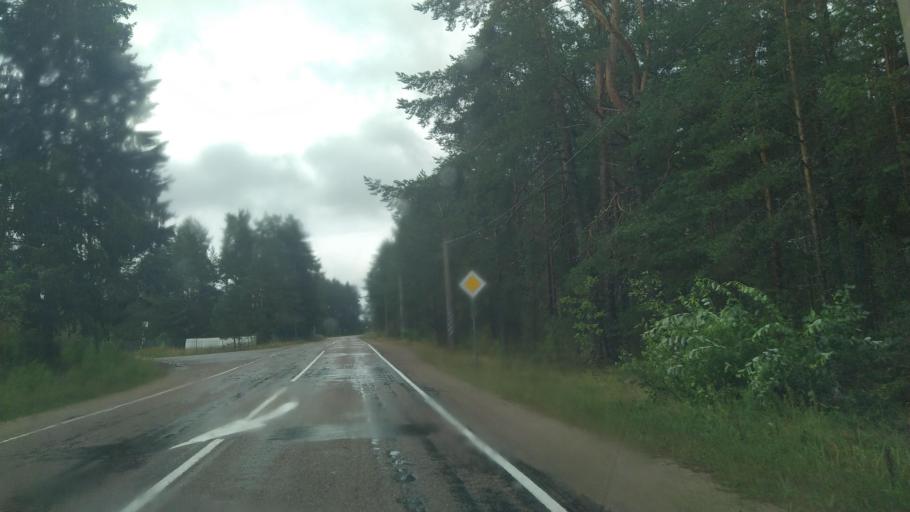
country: RU
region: Leningrad
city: Priozersk
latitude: 60.9658
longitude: 30.2872
